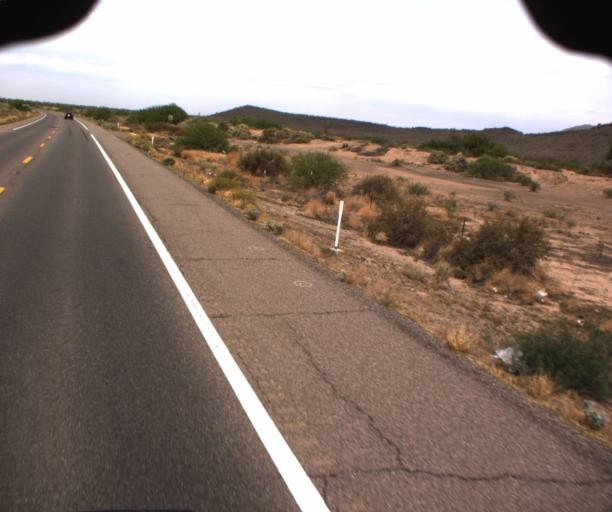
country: US
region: Arizona
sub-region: Pinal County
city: Sacaton
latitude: 33.1115
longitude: -111.7199
